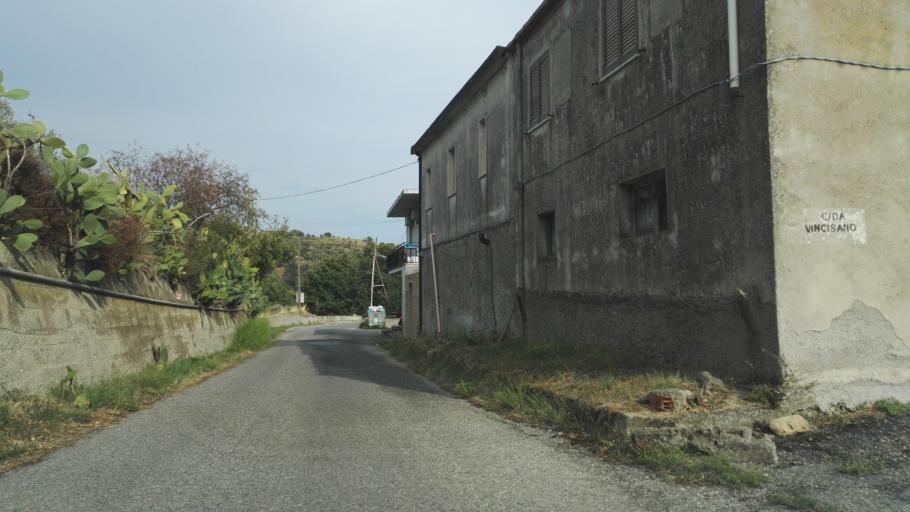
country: IT
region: Calabria
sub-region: Provincia di Reggio Calabria
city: Stignano
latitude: 38.4294
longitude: 16.4609
